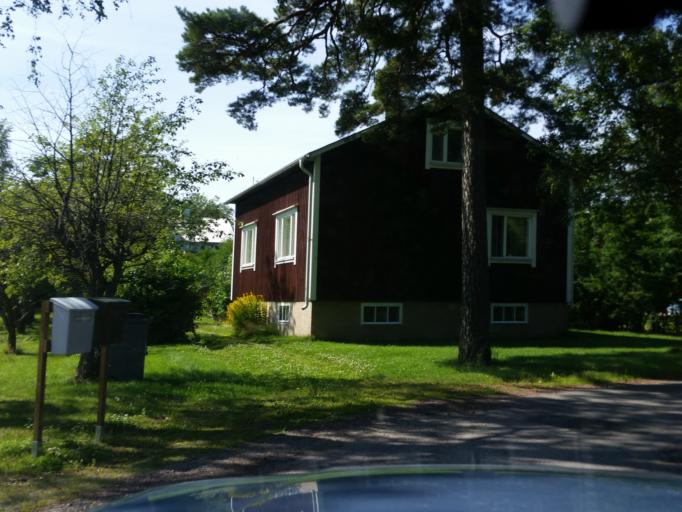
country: FI
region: Uusimaa
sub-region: Raaseporin
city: Hanko
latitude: 59.8324
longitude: 22.9479
